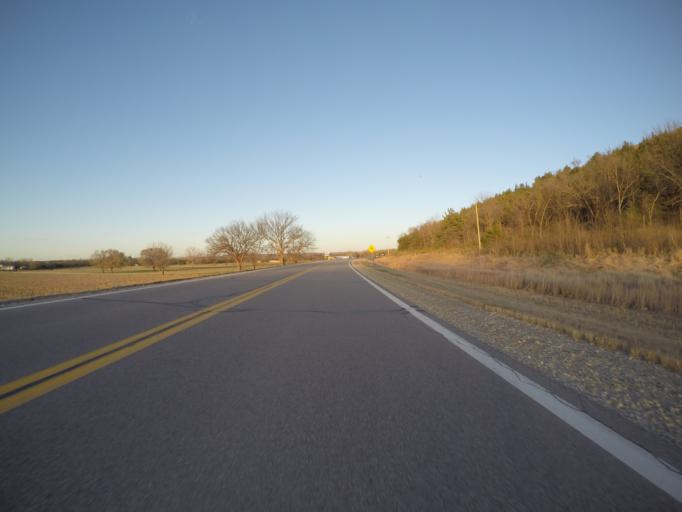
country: US
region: Kansas
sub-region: Riley County
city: Manhattan
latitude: 39.1167
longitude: -96.6069
